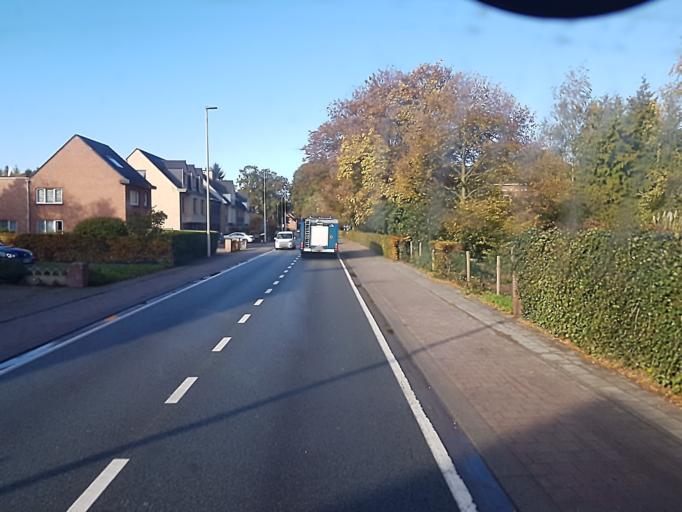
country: BE
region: Flanders
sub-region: Provincie Antwerpen
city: Brecht
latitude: 51.3474
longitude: 4.6427
